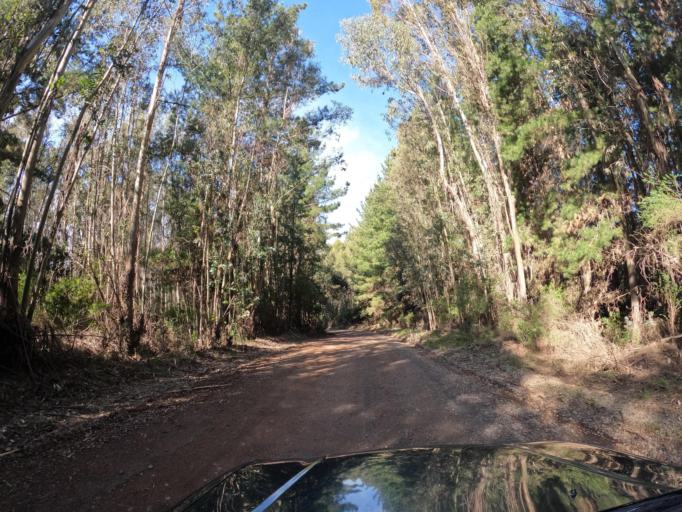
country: CL
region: Biobio
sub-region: Provincia de Biobio
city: La Laja
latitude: -37.0858
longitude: -72.7912
